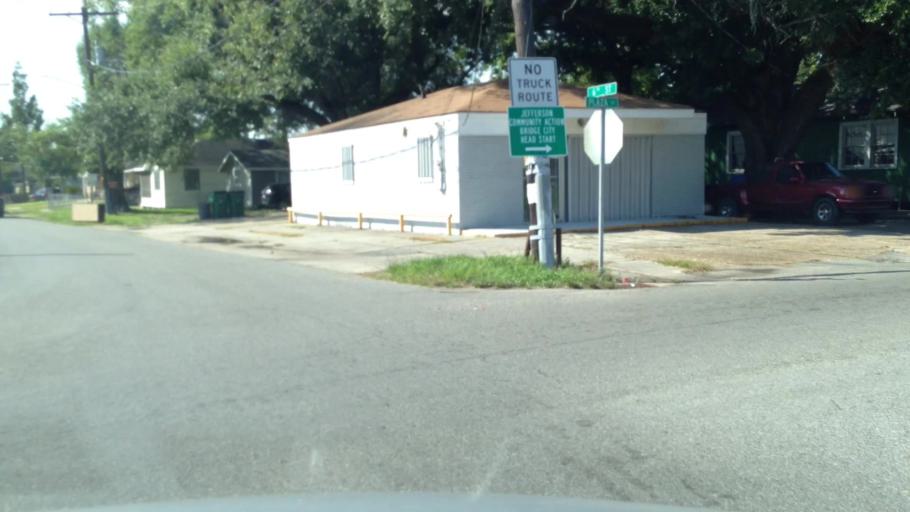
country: US
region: Louisiana
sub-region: Jefferson Parish
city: Bridge City
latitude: 29.9303
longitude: -90.1673
